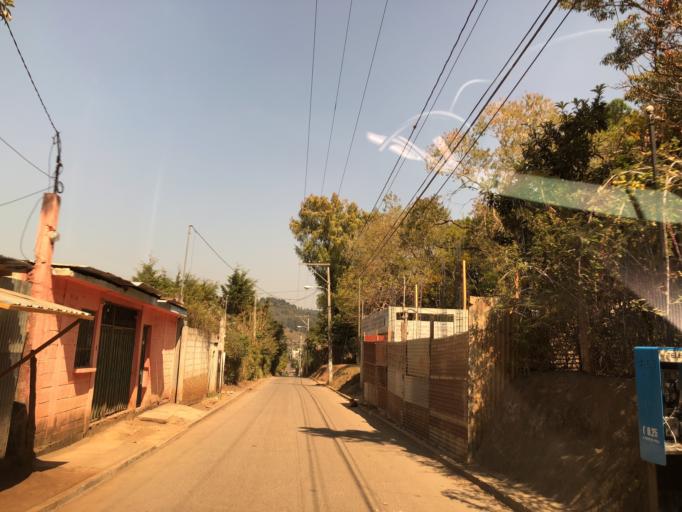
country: GT
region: Guatemala
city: Santa Catarina Pinula
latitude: 14.5365
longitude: -90.5073
